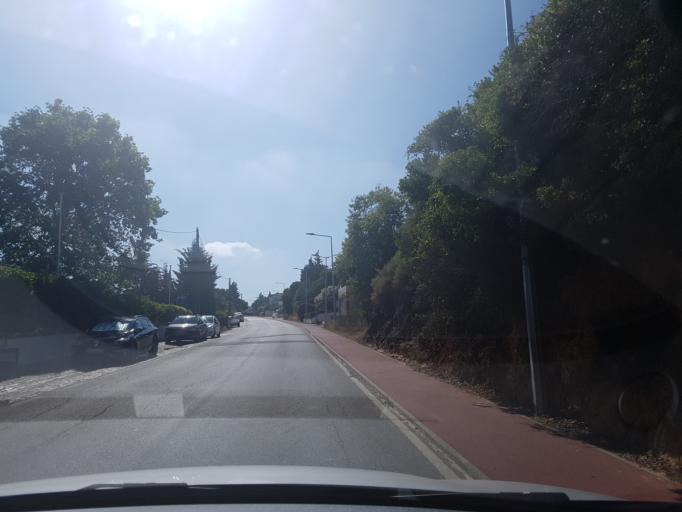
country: PT
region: Faro
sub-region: Lagoa
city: Carvoeiro
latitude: 37.0934
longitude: -8.4485
